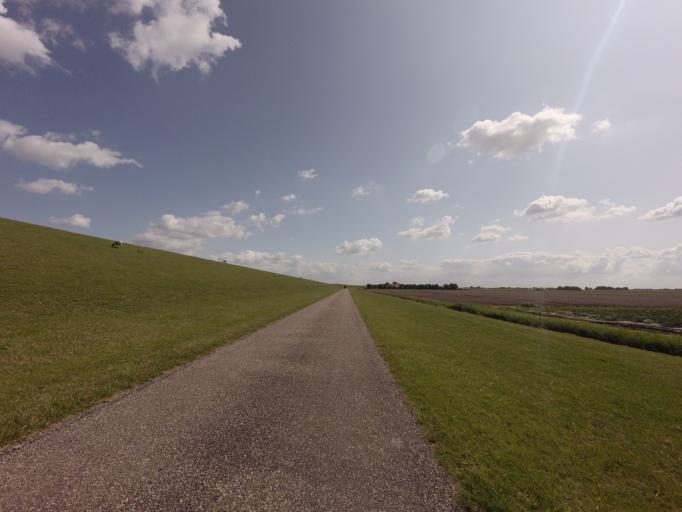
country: NL
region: Friesland
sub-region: Gemeente Ferwerderadiel
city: Hallum
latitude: 53.3242
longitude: 5.7324
